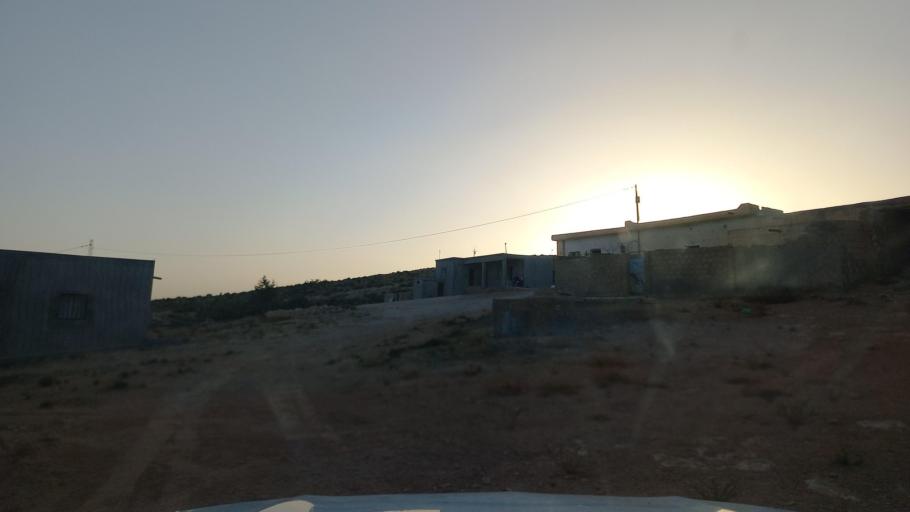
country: TN
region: Al Qasrayn
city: Sbiba
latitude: 35.3761
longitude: 9.0057
